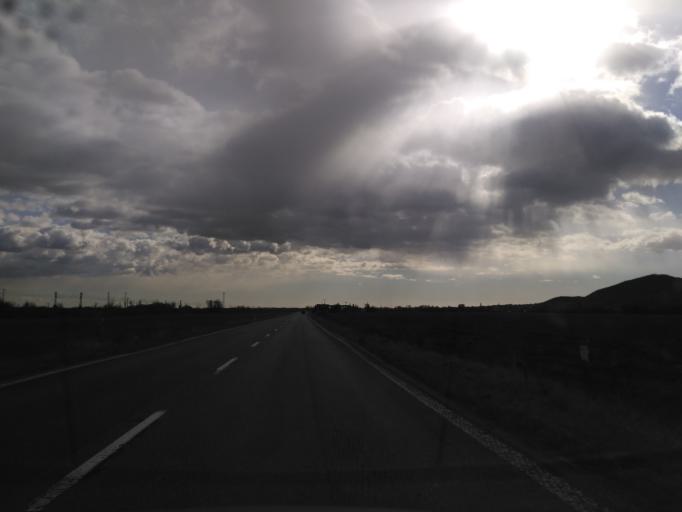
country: HU
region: Borsod-Abauj-Zemplen
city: Satoraljaujhely
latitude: 48.4332
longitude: 21.6578
